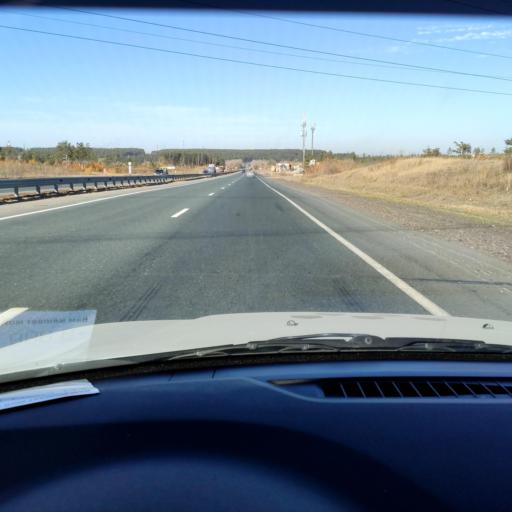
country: RU
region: Samara
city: Zhigulevsk
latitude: 53.5196
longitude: 49.5329
